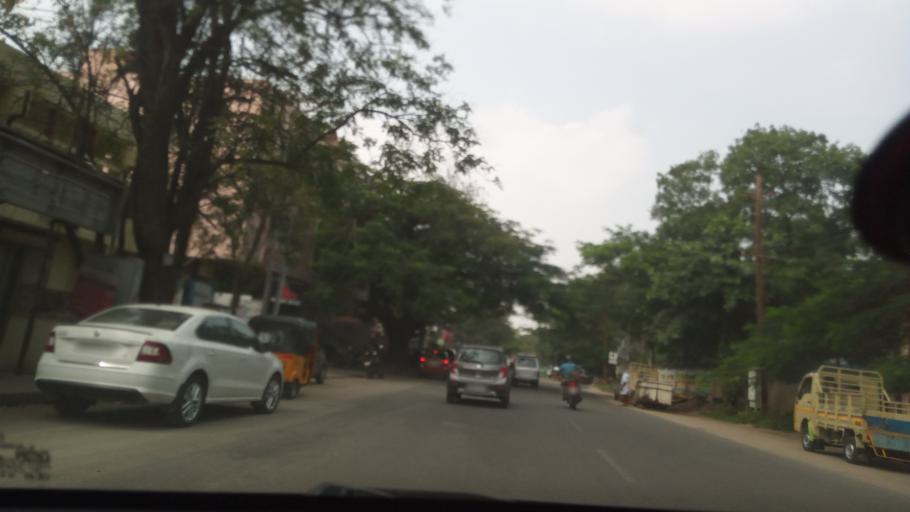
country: IN
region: Tamil Nadu
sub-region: Coimbatore
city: Coimbatore
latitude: 11.0173
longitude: 76.9582
